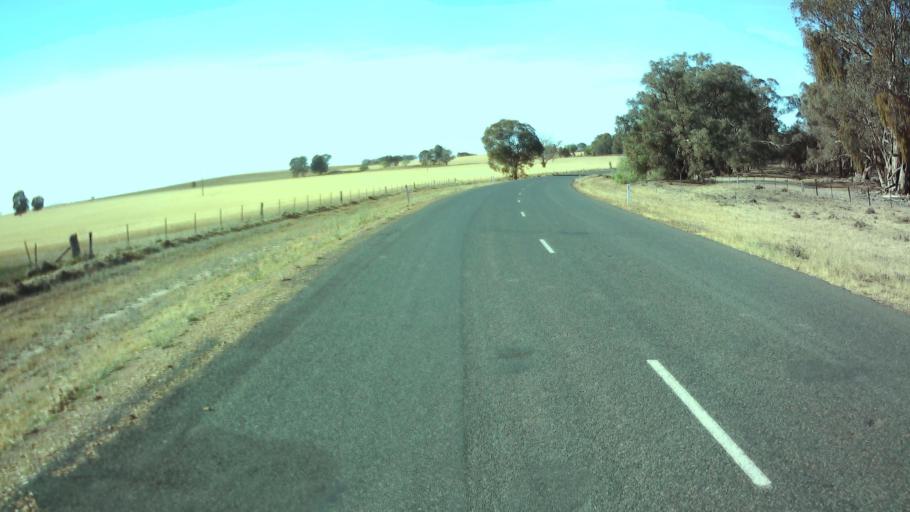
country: AU
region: New South Wales
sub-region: Weddin
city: Grenfell
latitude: -33.9849
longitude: 148.1408
